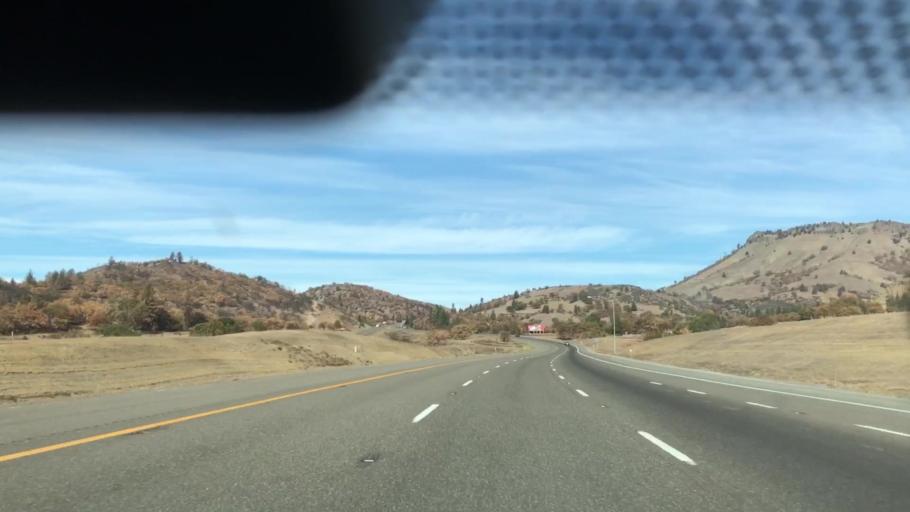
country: US
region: California
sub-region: Siskiyou County
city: Yreka
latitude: 41.9580
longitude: -122.5943
